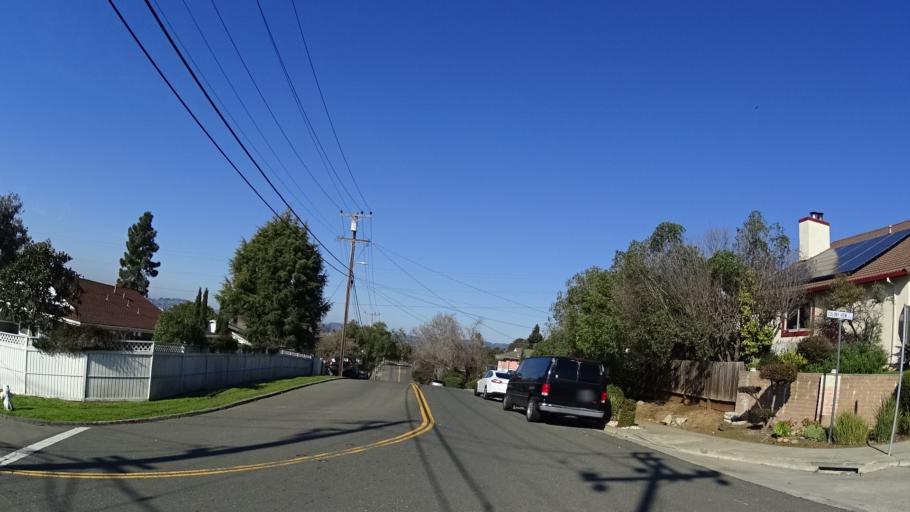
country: US
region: California
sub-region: Alameda County
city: Fairview
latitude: 37.6686
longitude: -122.0518
